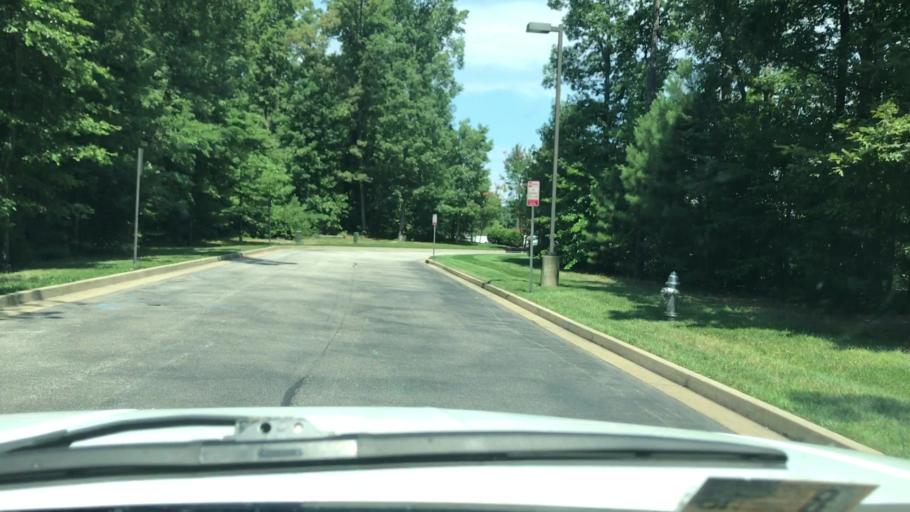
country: US
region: Virginia
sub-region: Henrico County
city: Short Pump
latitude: 37.6551
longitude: -77.5855
